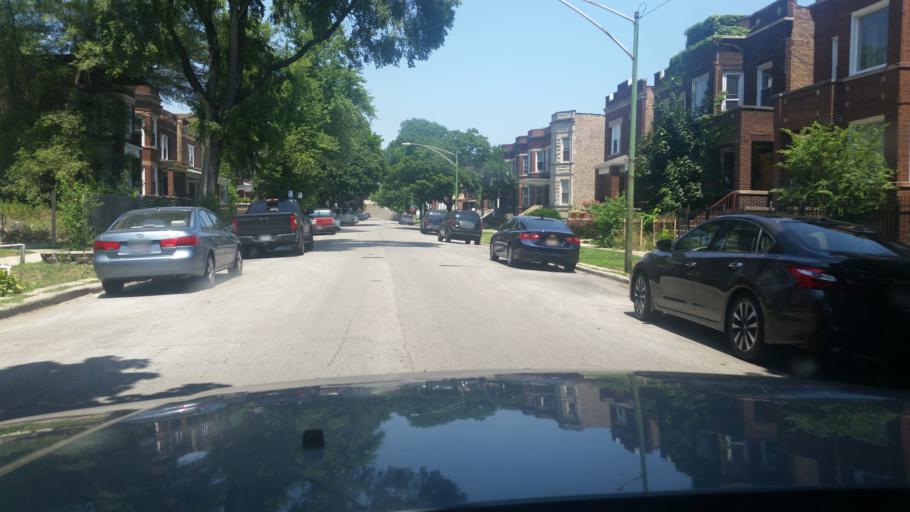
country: US
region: Illinois
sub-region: Cook County
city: Chicago
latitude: 41.7663
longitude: -87.6128
